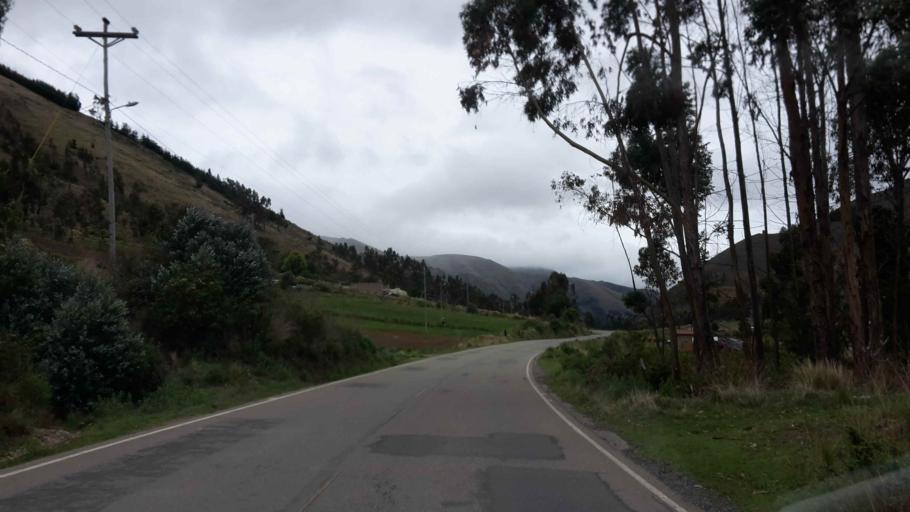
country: BO
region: Cochabamba
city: Arani
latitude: -17.4789
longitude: -65.5424
